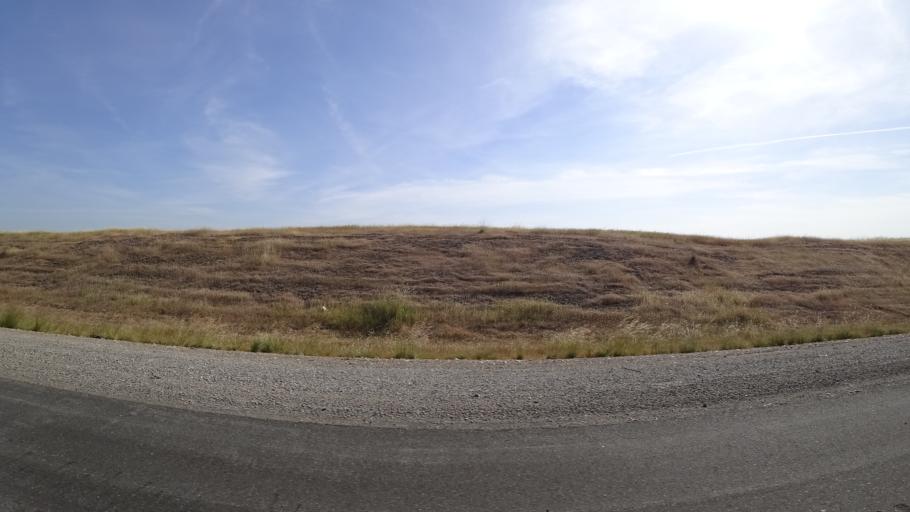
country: US
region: California
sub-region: Butte County
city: Thermalito
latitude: 39.5966
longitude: -121.6522
